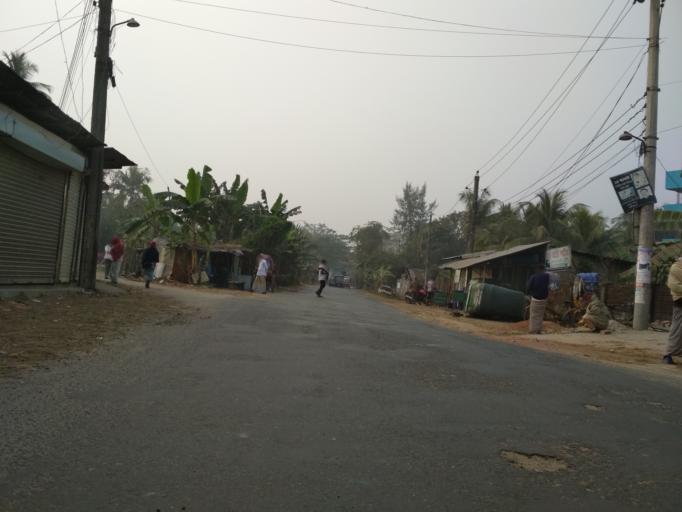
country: BD
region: Chittagong
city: Lakshmipur
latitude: 22.9219
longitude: 90.8366
